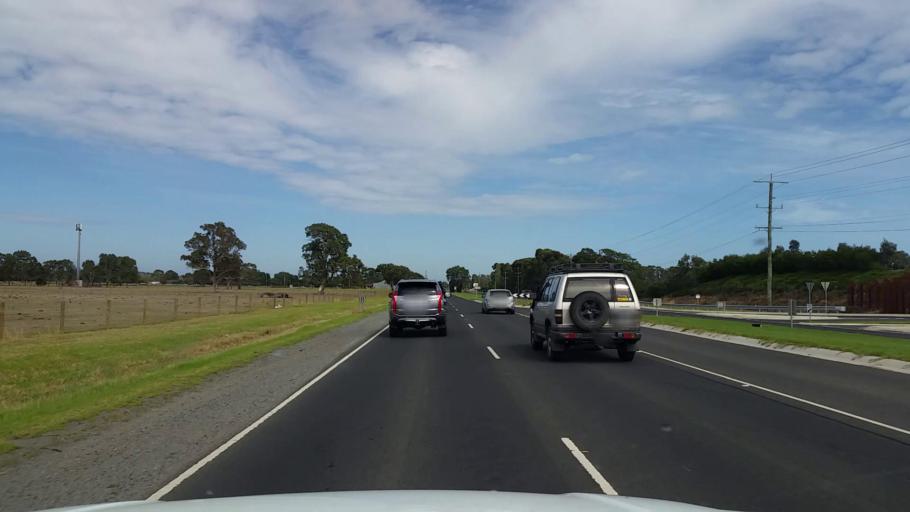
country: AU
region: Victoria
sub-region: Frankston
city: Sandhurst
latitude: -38.0664
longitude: 145.1996
